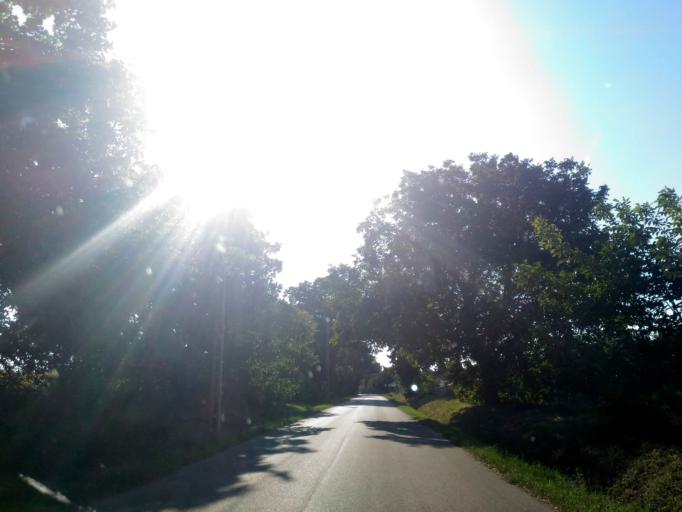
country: HU
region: Somogy
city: Balatonszarszo
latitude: 46.8069
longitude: 17.7892
